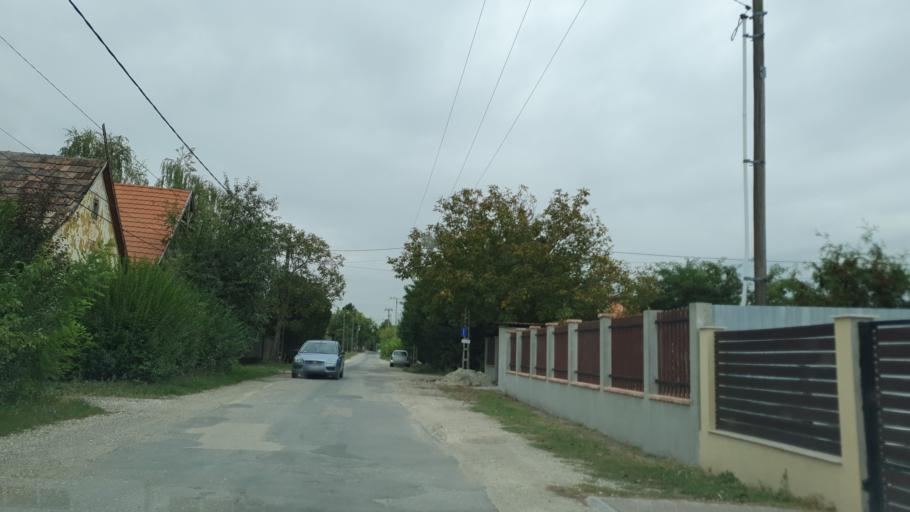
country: HU
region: Budapest
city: Budapest XXIII. keruelet
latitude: 47.3884
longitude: 19.0919
